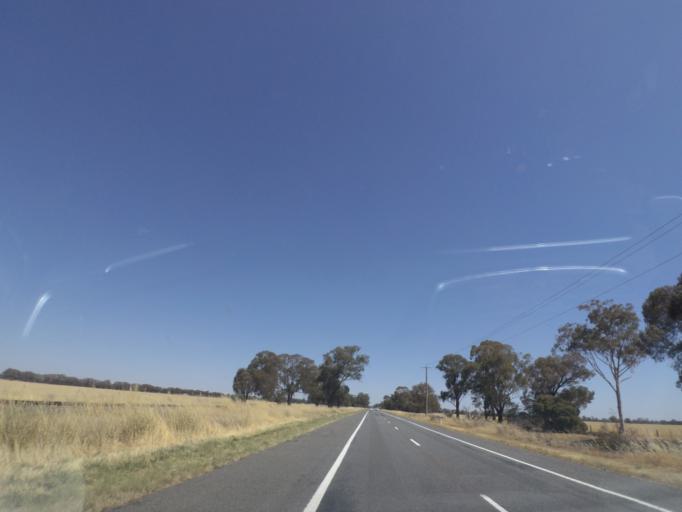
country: AU
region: Victoria
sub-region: Greater Shepparton
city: Shepparton
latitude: -36.2032
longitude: 145.4318
